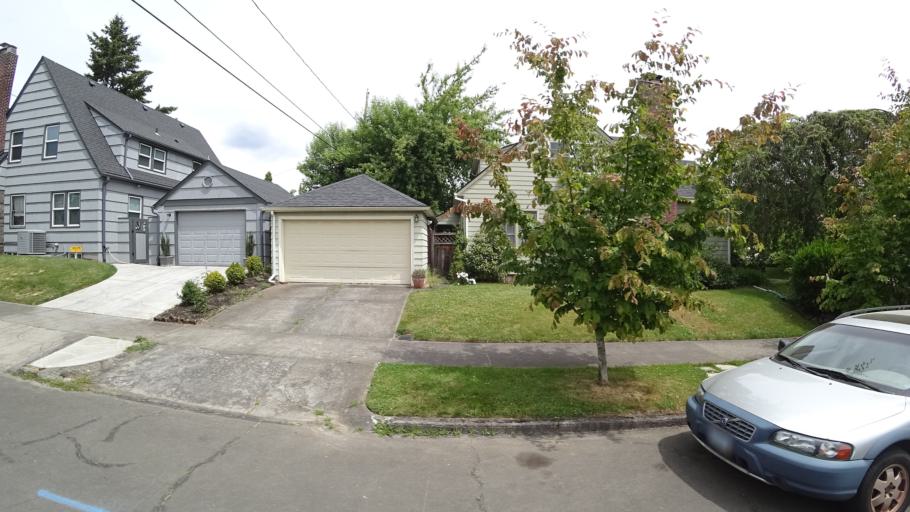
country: US
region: Oregon
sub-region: Multnomah County
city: Portland
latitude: 45.5281
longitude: -122.6173
